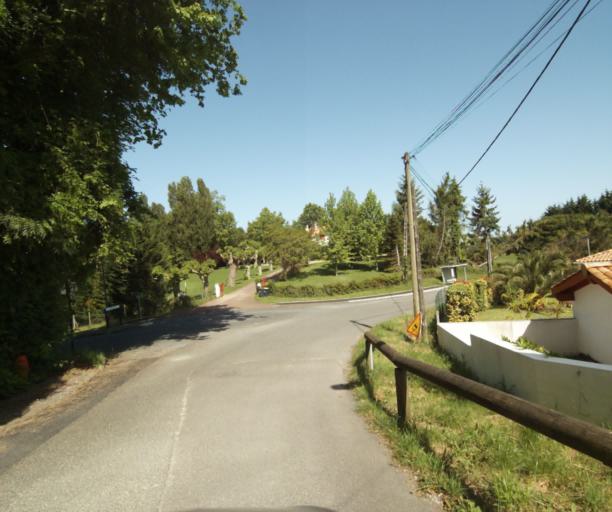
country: FR
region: Aquitaine
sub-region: Departement des Pyrenees-Atlantiques
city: Villefranque
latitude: 43.4574
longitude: -1.4492
